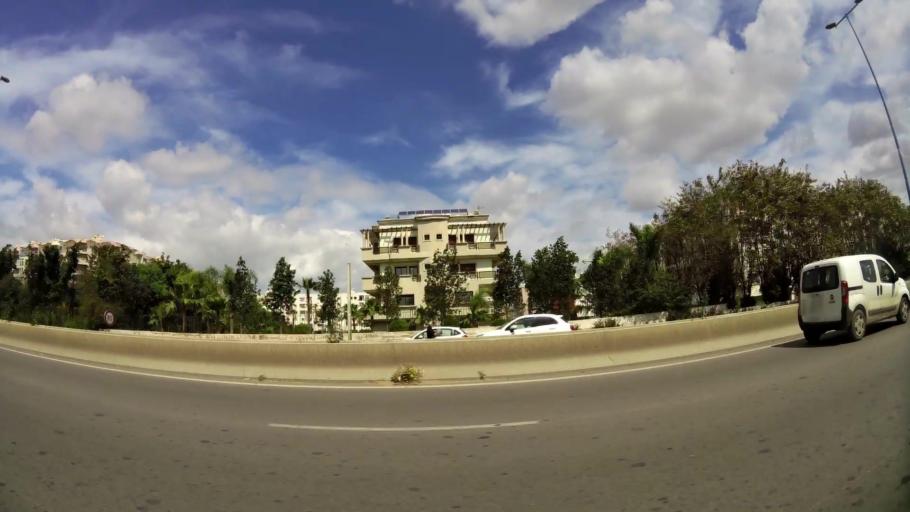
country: MA
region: Grand Casablanca
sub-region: Casablanca
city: Casablanca
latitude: 33.5526
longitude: -7.6272
